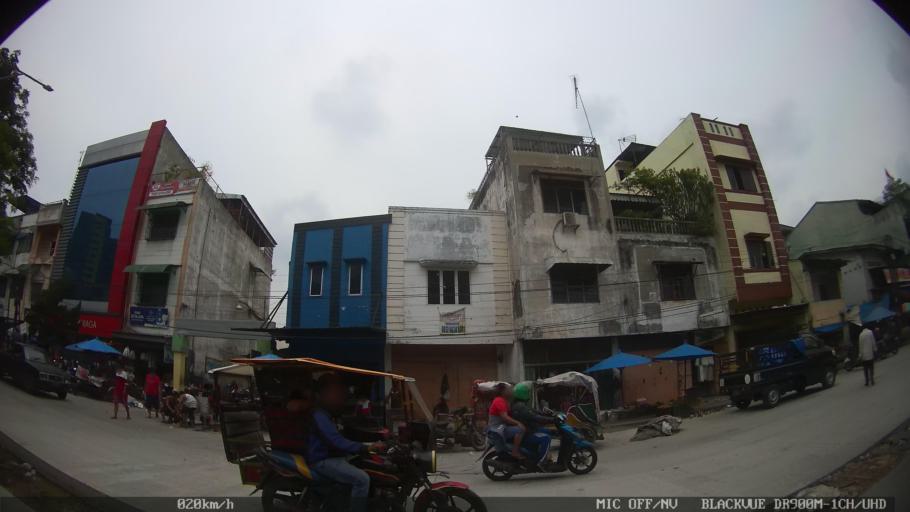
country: ID
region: North Sumatra
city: Medan
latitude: 3.5834
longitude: 98.7047
